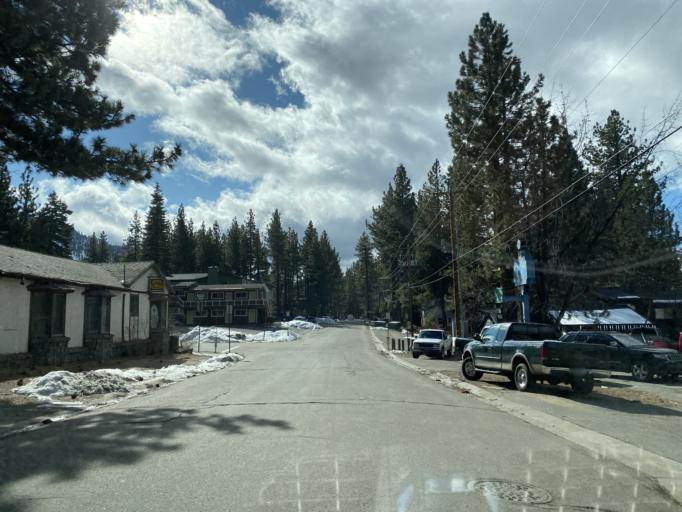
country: US
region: Nevada
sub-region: Douglas County
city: Kingsbury
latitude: 38.9595
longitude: -119.9457
